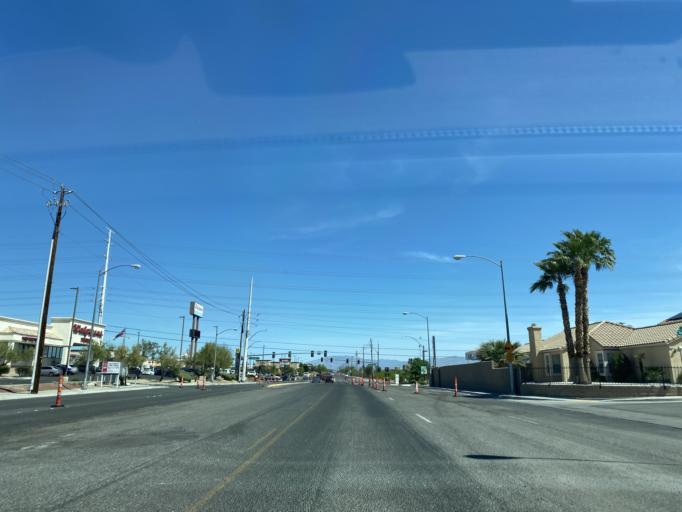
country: US
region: Nevada
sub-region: Clark County
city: Spring Valley
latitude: 36.1133
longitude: -115.2609
